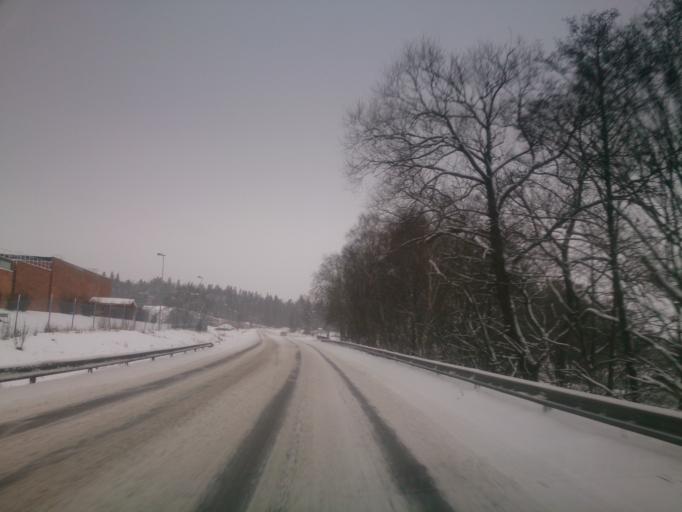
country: SE
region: OEstergoetland
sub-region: Norrkopings Kommun
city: Skarblacka
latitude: 58.5857
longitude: 15.8912
